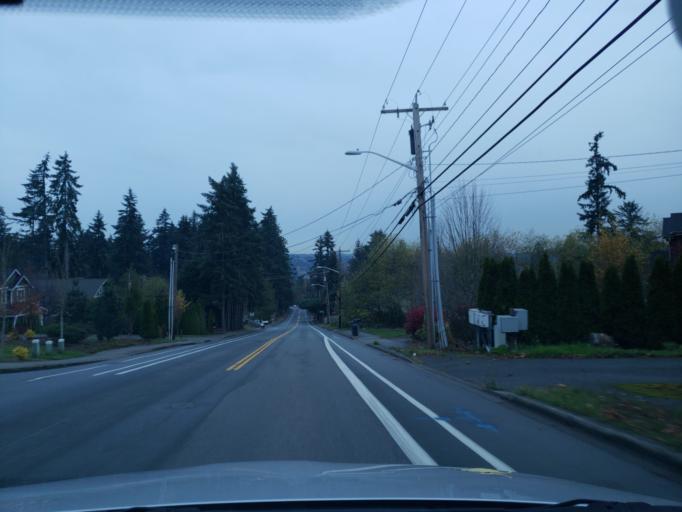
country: US
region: Washington
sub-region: King County
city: Kenmore
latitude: 47.7470
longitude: -122.2307
